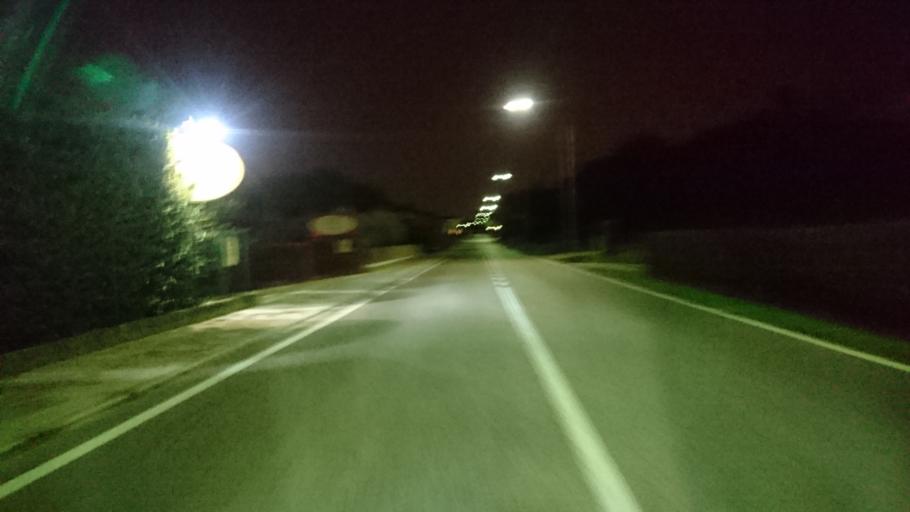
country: IT
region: Veneto
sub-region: Provincia di Treviso
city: Maser
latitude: 45.8155
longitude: 11.9832
